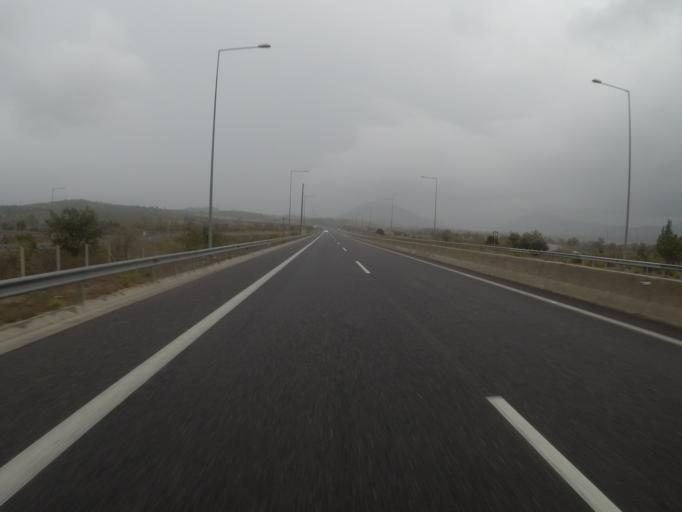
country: GR
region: Peloponnese
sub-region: Nomos Arkadias
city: Megalopoli
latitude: 37.3903
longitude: 22.2615
